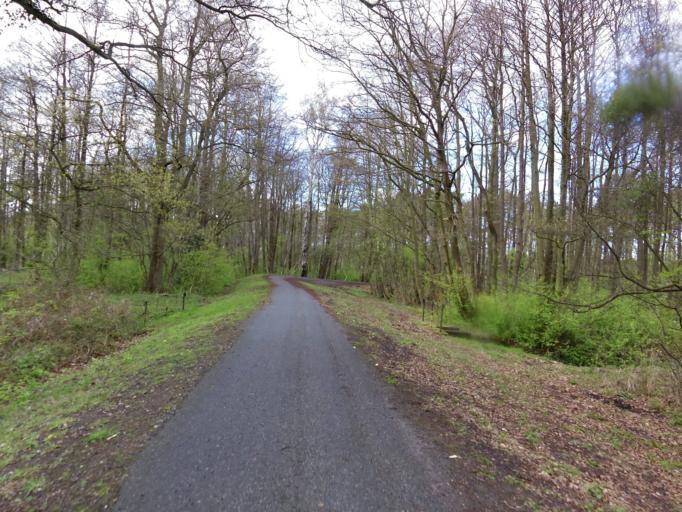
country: DE
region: Mecklenburg-Vorpommern
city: Ostseebad Prerow
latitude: 54.4476
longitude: 12.5763
